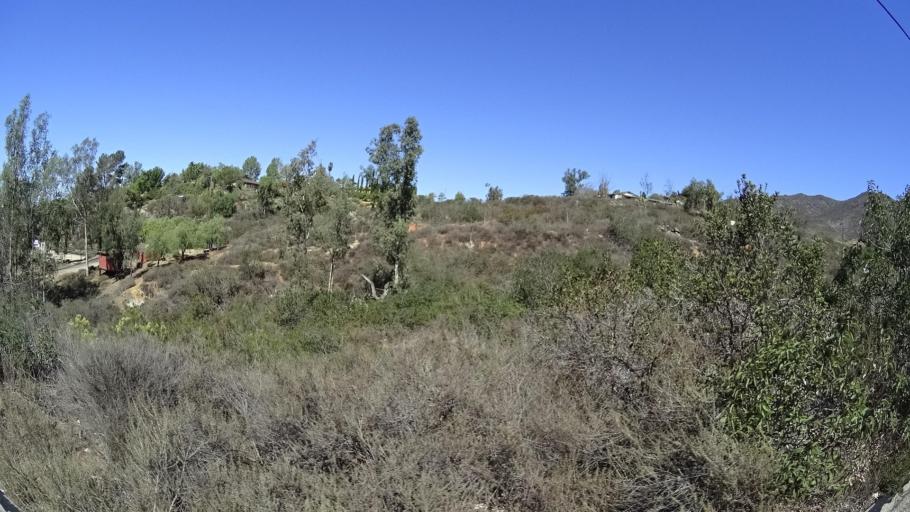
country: US
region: California
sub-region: San Diego County
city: Jamul
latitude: 32.7393
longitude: -116.8731
